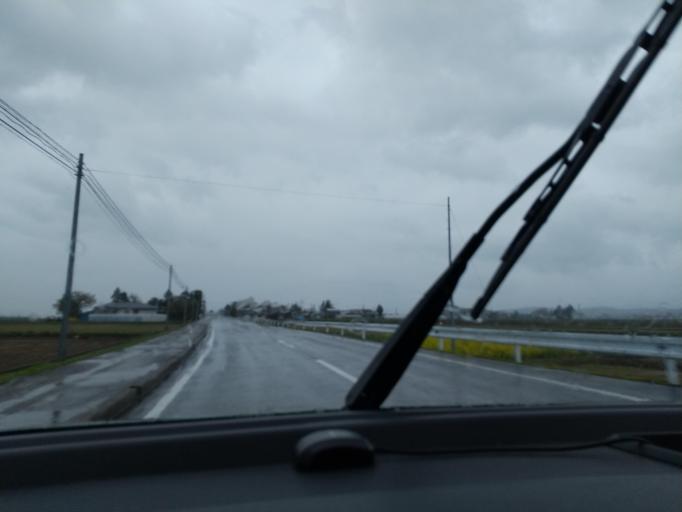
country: JP
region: Akita
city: Omagari
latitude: 39.4066
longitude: 140.5386
